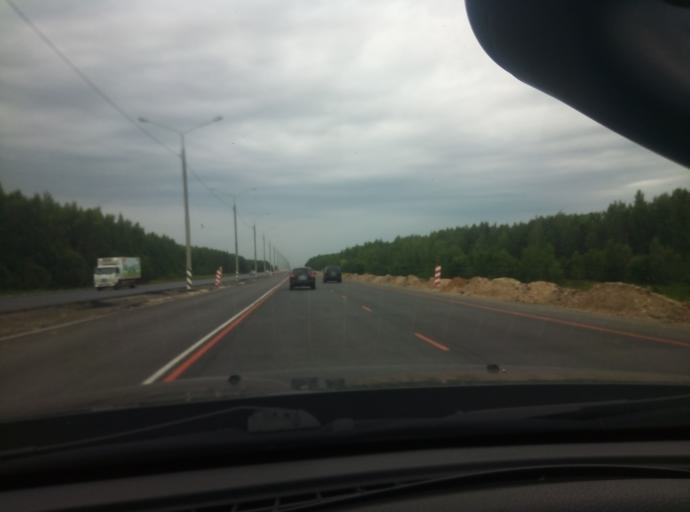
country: RU
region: Tula
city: Yasnogorsk
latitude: 54.5419
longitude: 37.5178
